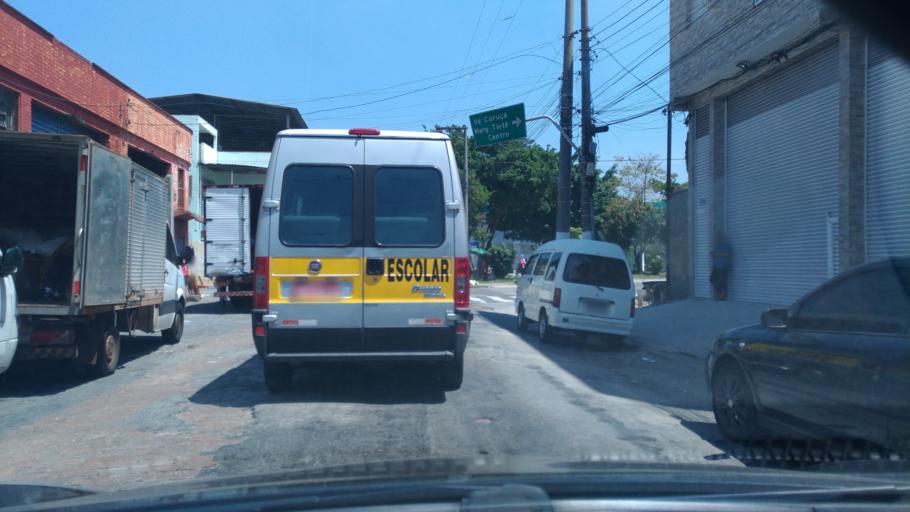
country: BR
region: Sao Paulo
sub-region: Sao Paulo
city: Sao Paulo
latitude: -23.5193
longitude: -46.5801
